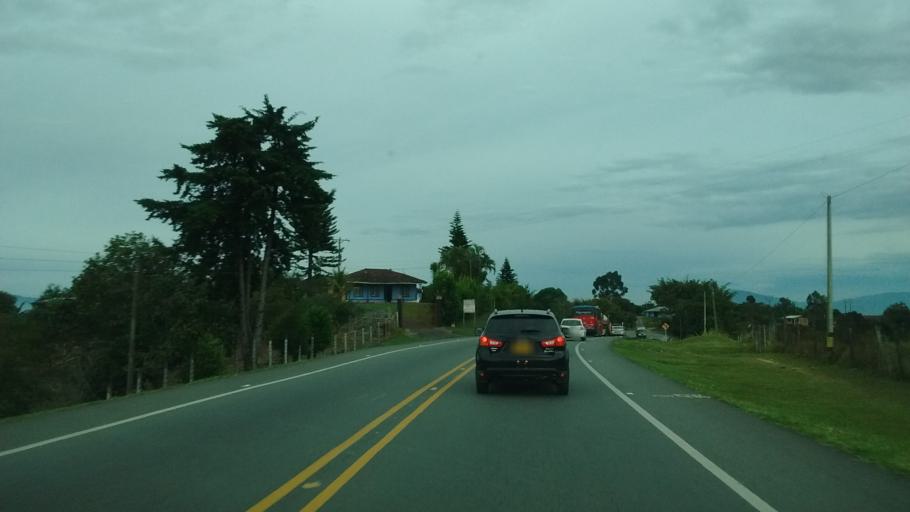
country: CO
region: Cauca
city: Morales
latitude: 2.7479
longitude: -76.5499
